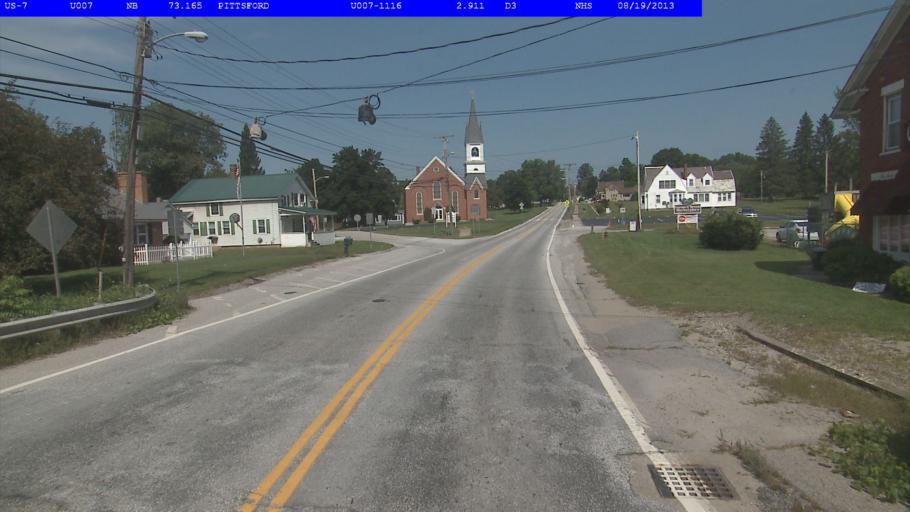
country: US
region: Vermont
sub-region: Rutland County
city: Rutland
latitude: 43.7013
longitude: -73.0113
